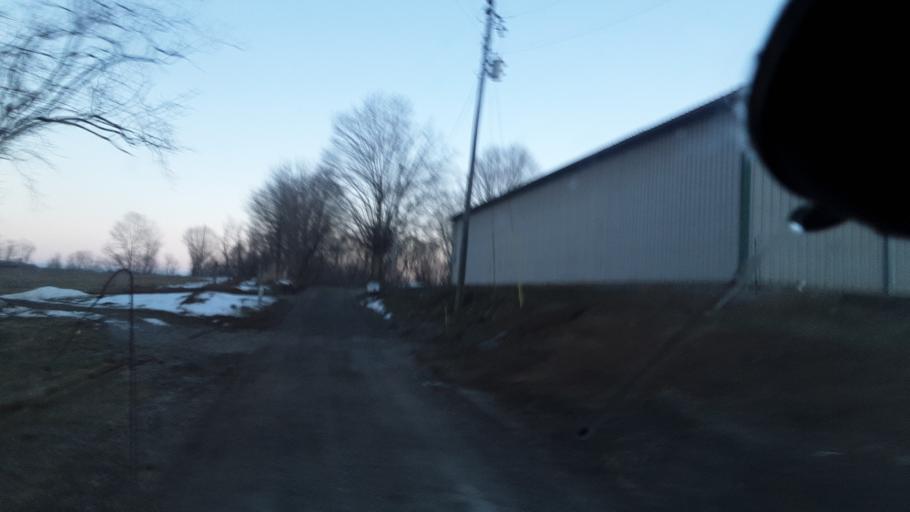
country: US
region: Ohio
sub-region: Perry County
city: Somerset
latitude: 39.7141
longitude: -82.3099
